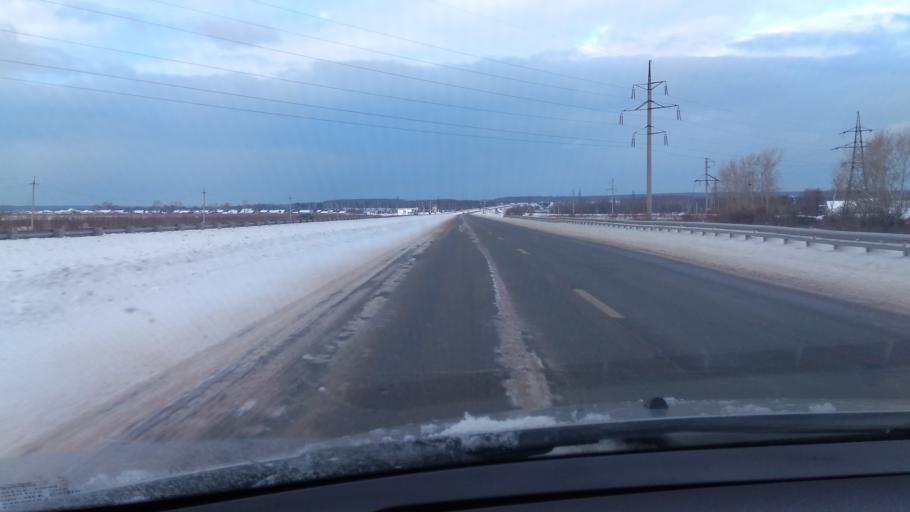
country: RU
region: Sverdlovsk
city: Tsementnyy
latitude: 57.4905
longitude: 60.1782
